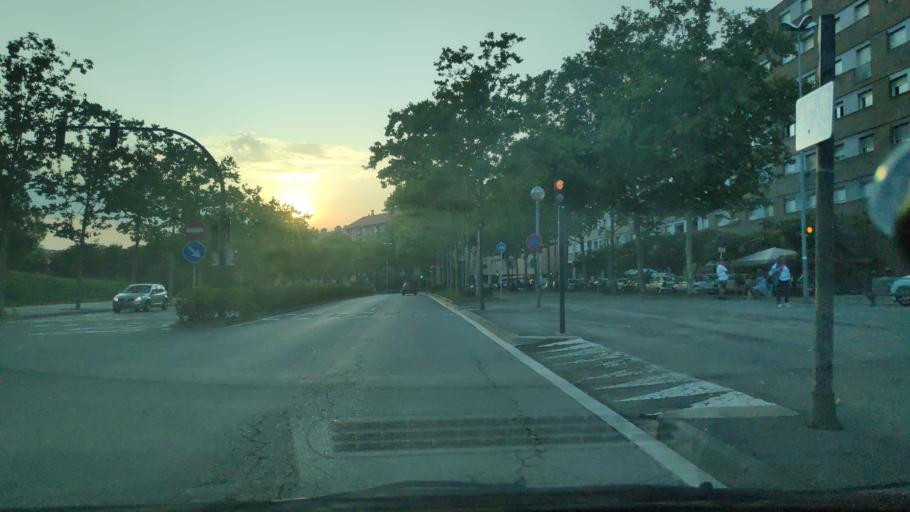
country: ES
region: Catalonia
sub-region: Provincia de Barcelona
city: Cerdanyola del Valles
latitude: 41.4836
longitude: 2.1504
